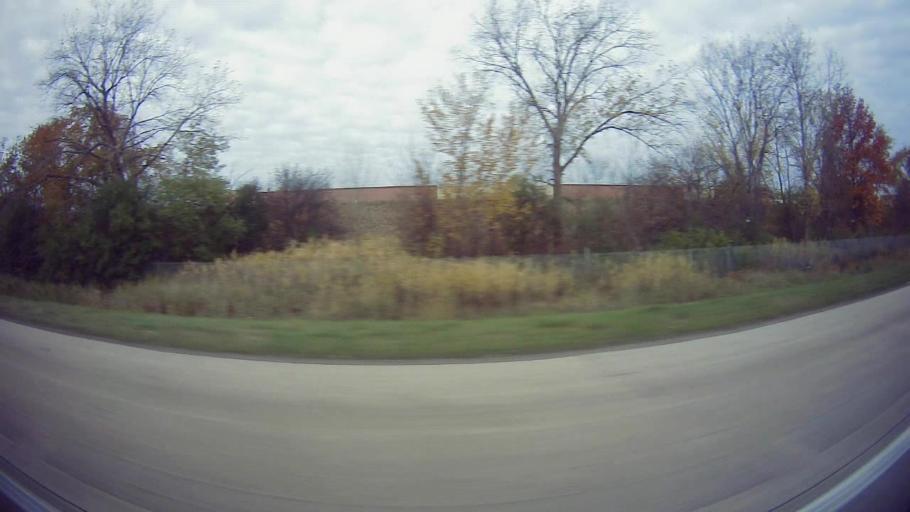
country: US
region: Michigan
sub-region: Wayne County
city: Allen Park
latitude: 42.2780
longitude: -83.2026
